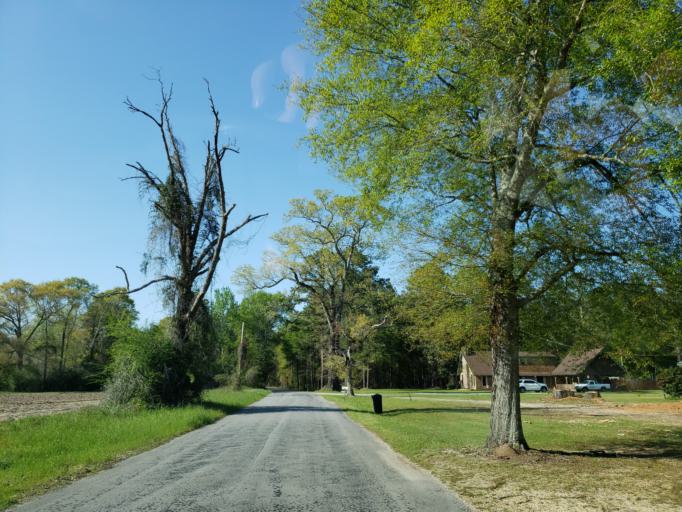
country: US
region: Mississippi
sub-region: Smith County
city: Taylorsville
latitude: 31.6977
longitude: -89.4136
